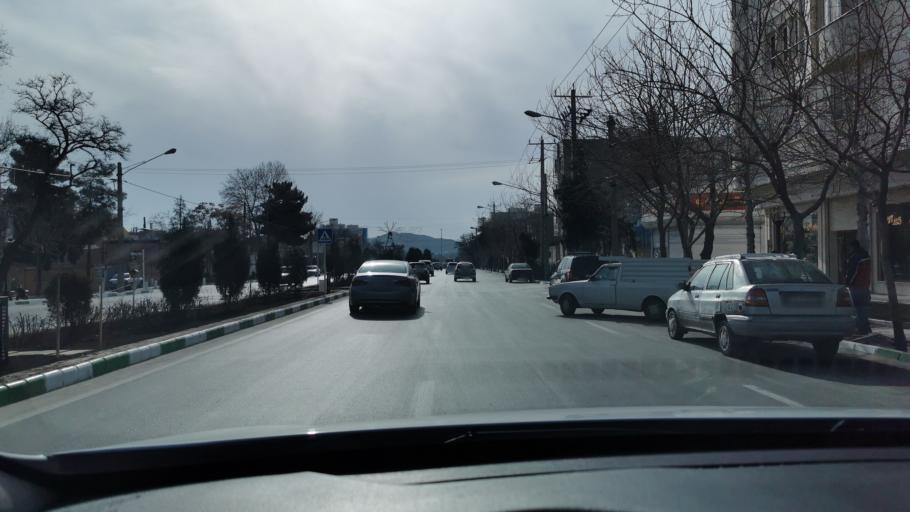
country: IR
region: Razavi Khorasan
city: Mashhad
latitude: 36.2867
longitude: 59.5449
